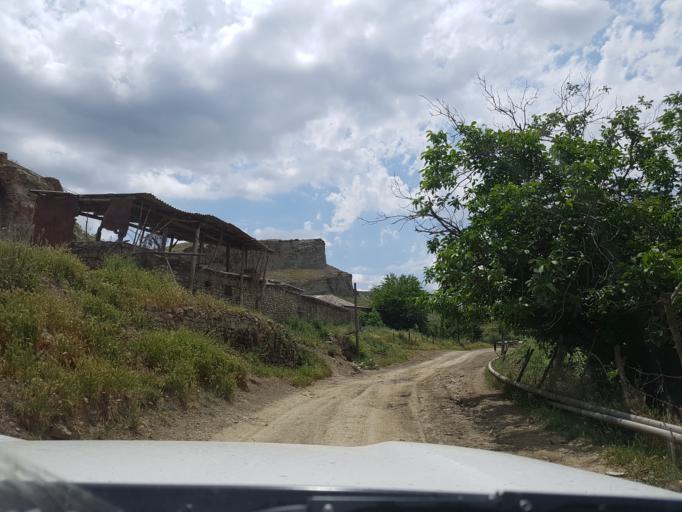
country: TM
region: Ahal
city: Baharly
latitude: 38.2038
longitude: 57.0017
